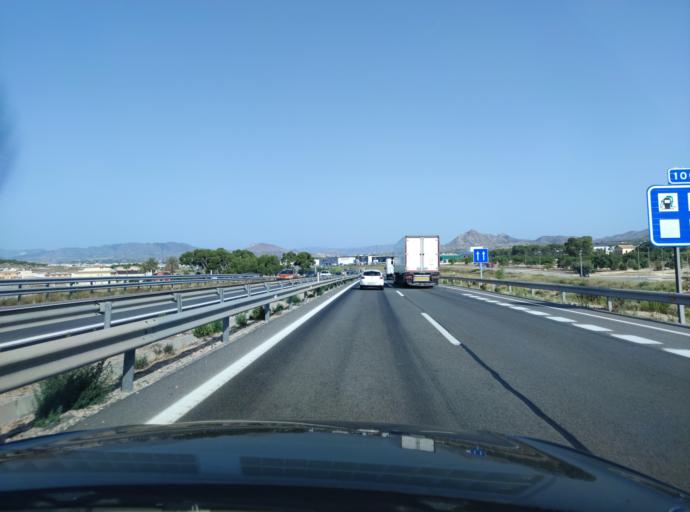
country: ES
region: Valencia
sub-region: Provincia de Alicante
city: Monforte del Cid
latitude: 38.3852
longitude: -0.7237
